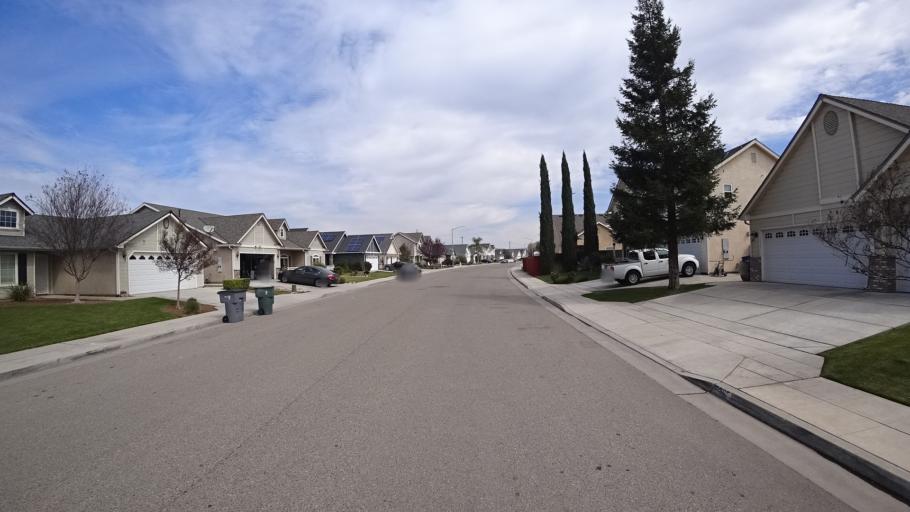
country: US
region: California
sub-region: Fresno County
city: Biola
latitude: 36.8354
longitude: -119.8959
